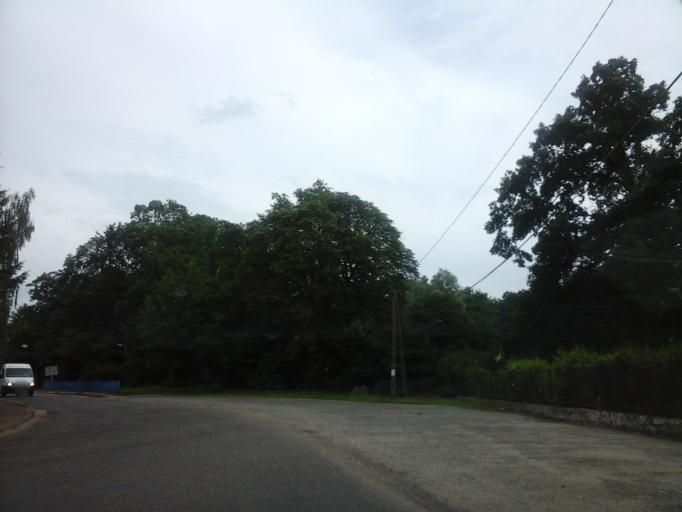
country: PL
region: West Pomeranian Voivodeship
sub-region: Powiat stargardzki
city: Marianowo
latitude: 53.3392
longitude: 15.1921
